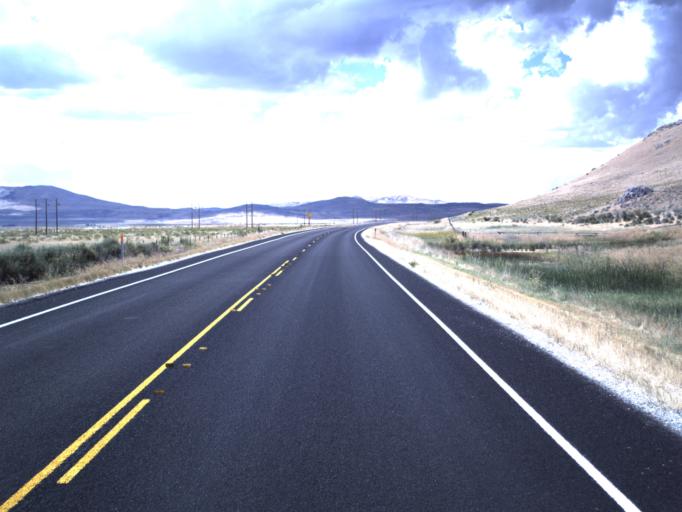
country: US
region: Utah
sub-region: Box Elder County
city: Tremonton
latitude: 41.6136
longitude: -112.3722
